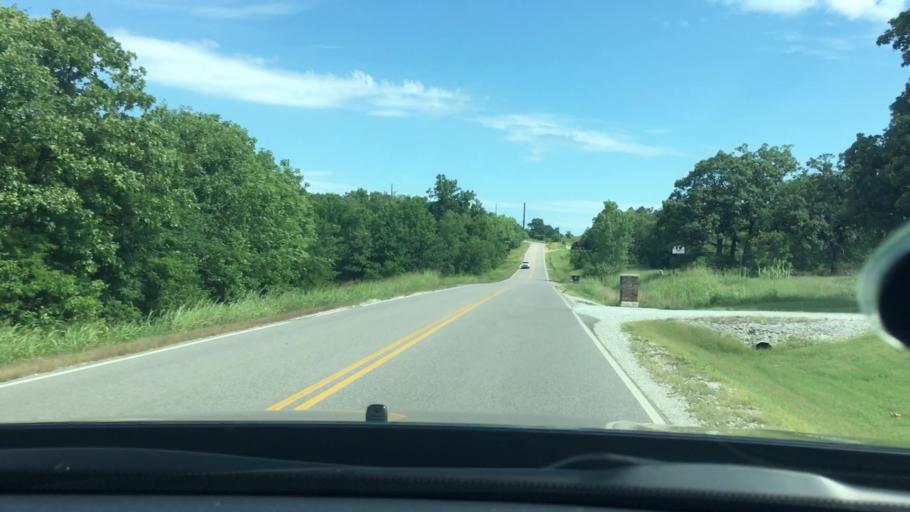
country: US
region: Oklahoma
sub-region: Pontotoc County
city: Ada
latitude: 34.7682
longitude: -96.5821
